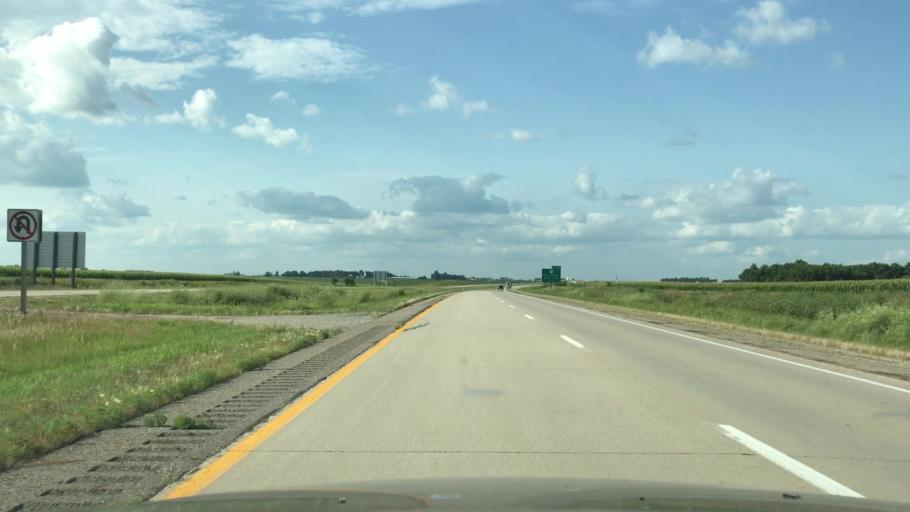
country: US
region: Iowa
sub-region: Osceola County
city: Sibley
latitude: 43.4143
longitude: -95.7170
